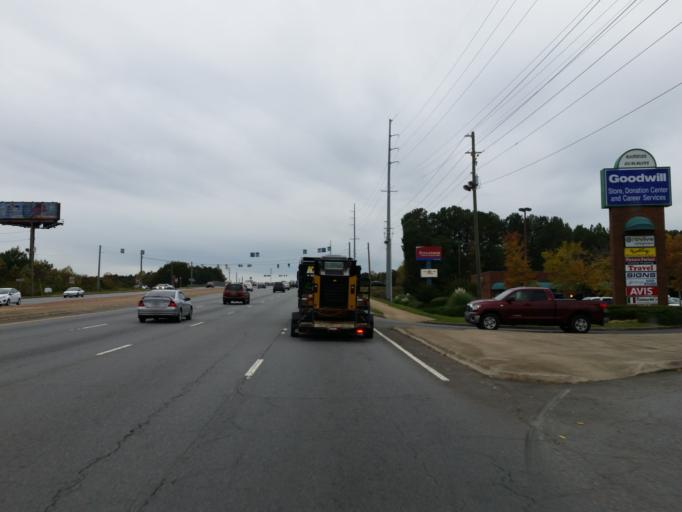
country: US
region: Georgia
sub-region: Cherokee County
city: Woodstock
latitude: 34.0860
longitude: -84.5320
